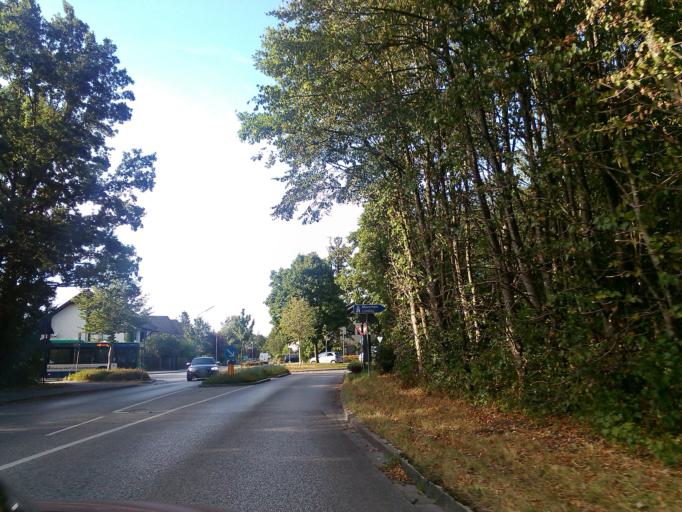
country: DE
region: Bavaria
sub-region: Upper Bavaria
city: Germering
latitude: 48.1178
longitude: 11.3746
